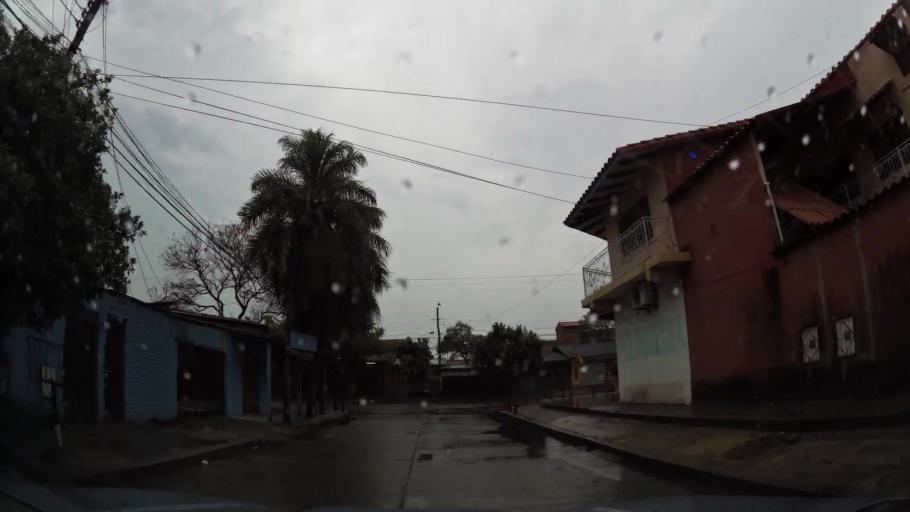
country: BO
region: Santa Cruz
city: Santa Cruz de la Sierra
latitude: -17.7724
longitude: -63.1497
